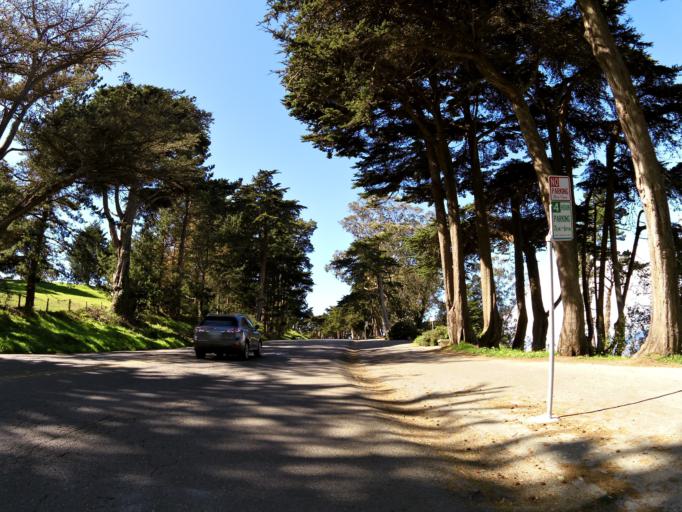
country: US
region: California
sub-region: Marin County
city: Sausalito
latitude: 37.7859
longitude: -122.4962
